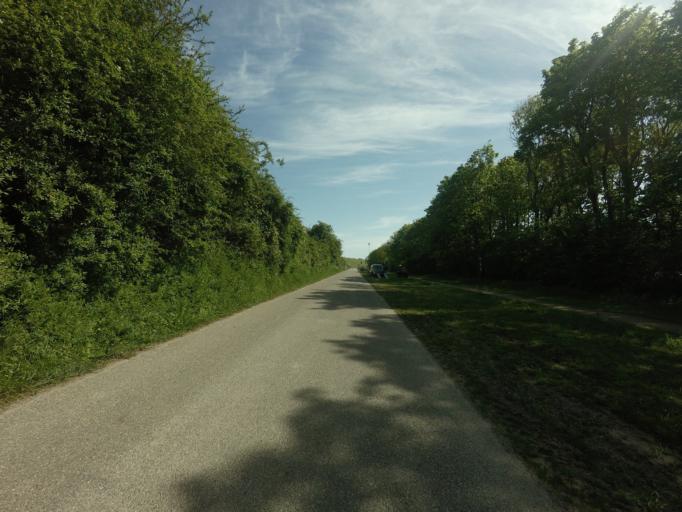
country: NL
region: Zeeland
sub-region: Gemeente Noord-Beveland
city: Kamperland
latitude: 51.5934
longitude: 3.6675
